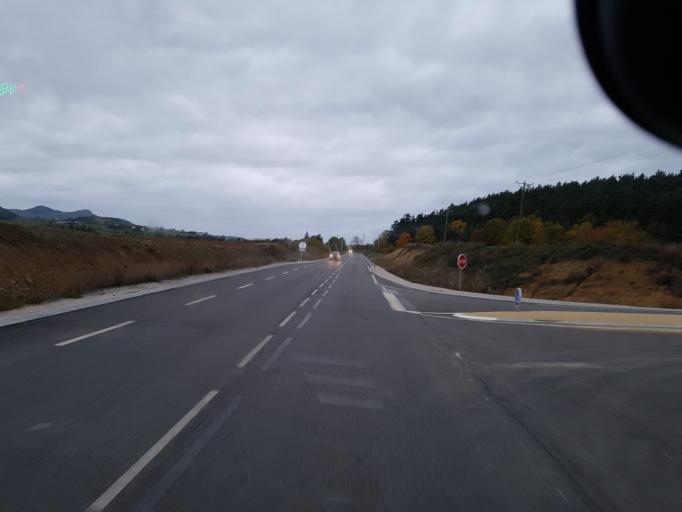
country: FR
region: Auvergne
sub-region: Departement de la Haute-Loire
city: Yssingeaux
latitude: 45.1640
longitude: 4.1520
